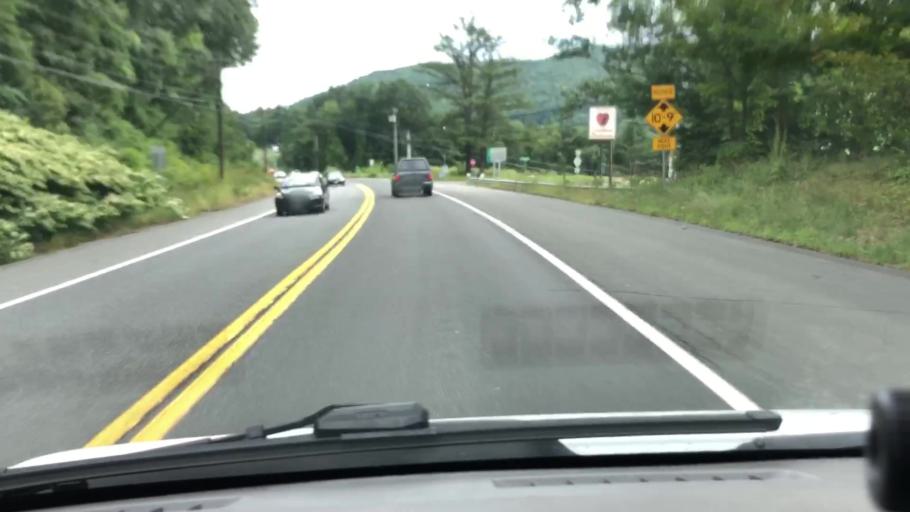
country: US
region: Massachusetts
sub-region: Franklin County
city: Shelburne Falls
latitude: 42.6015
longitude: -72.7307
